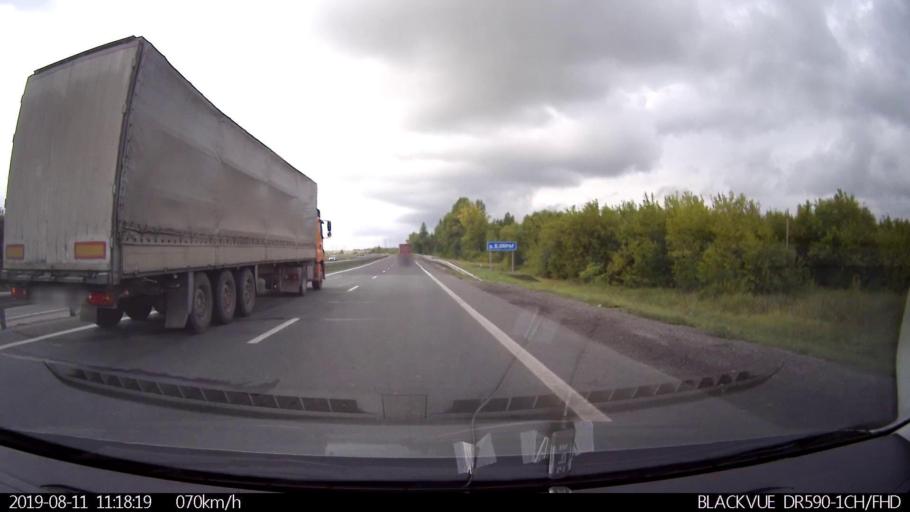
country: RU
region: Ulyanovsk
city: Novoul'yanovsk
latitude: 54.1809
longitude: 48.2692
